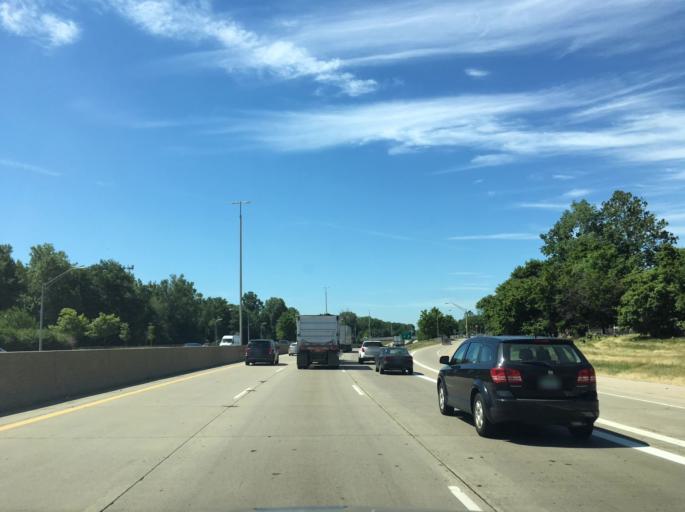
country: US
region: Michigan
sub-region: Wayne County
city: Melvindale
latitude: 42.2928
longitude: -83.2049
